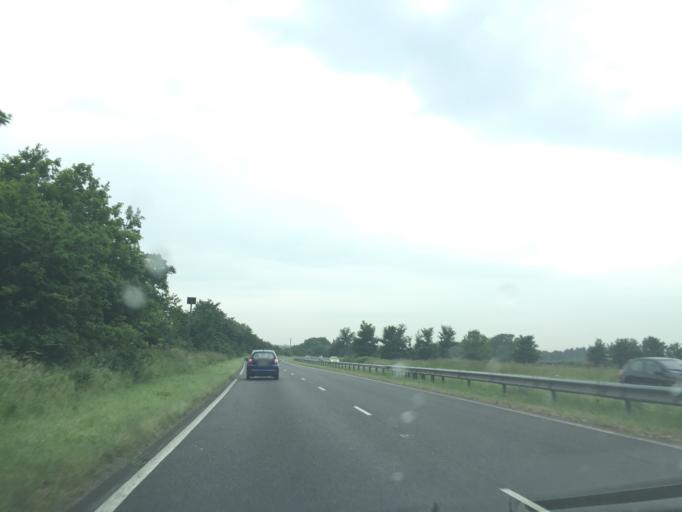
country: GB
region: England
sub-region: Dorset
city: Lytchett Matravers
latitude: 50.7361
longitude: -2.0504
